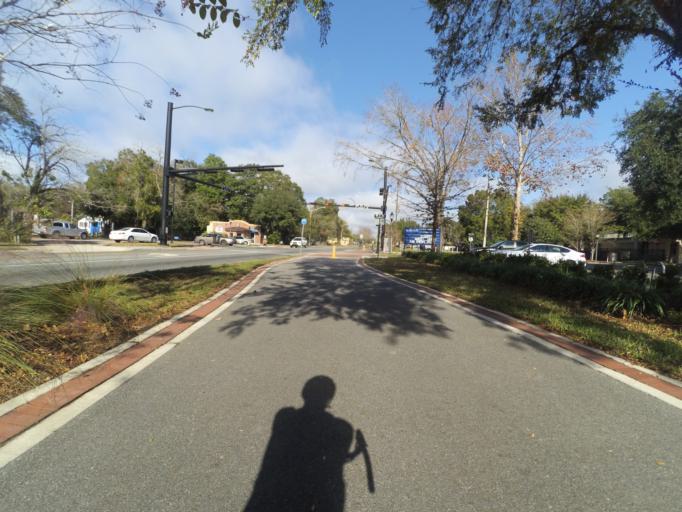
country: US
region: Florida
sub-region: Alachua County
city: Gainesville
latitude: 29.6553
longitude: -82.3307
